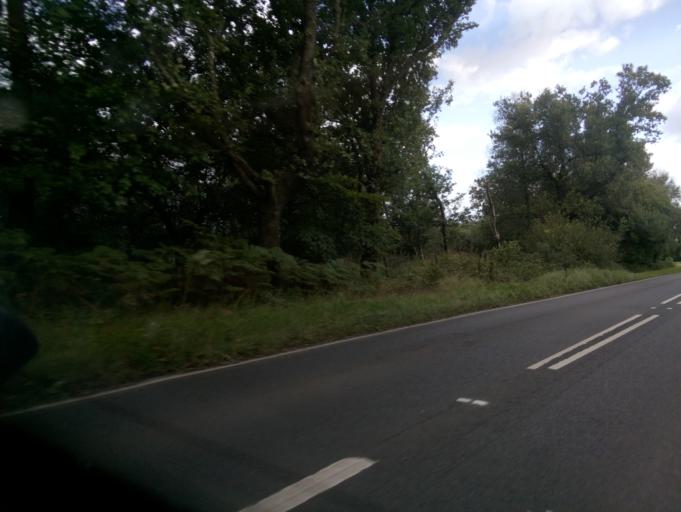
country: GB
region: England
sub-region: Devon
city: Honiton
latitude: 50.7601
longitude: -3.2123
